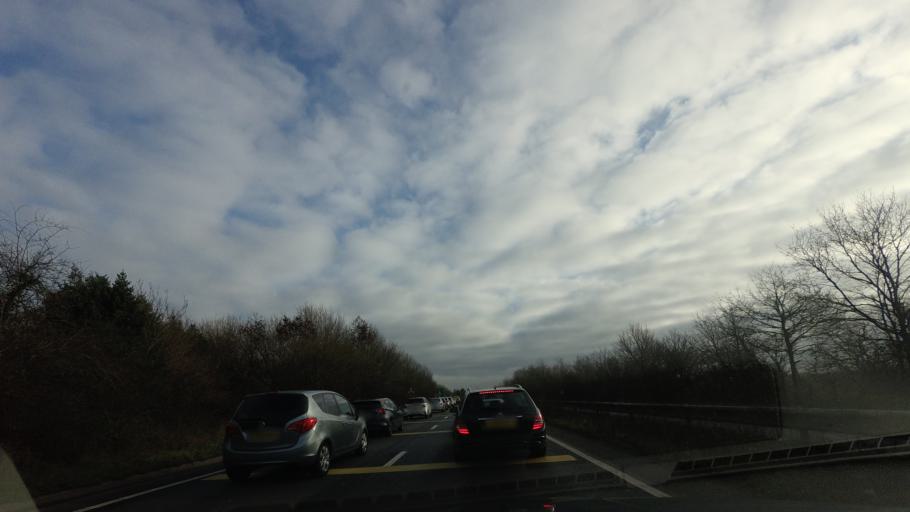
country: GB
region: England
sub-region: Kent
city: Pembury
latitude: 51.1364
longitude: 0.3444
